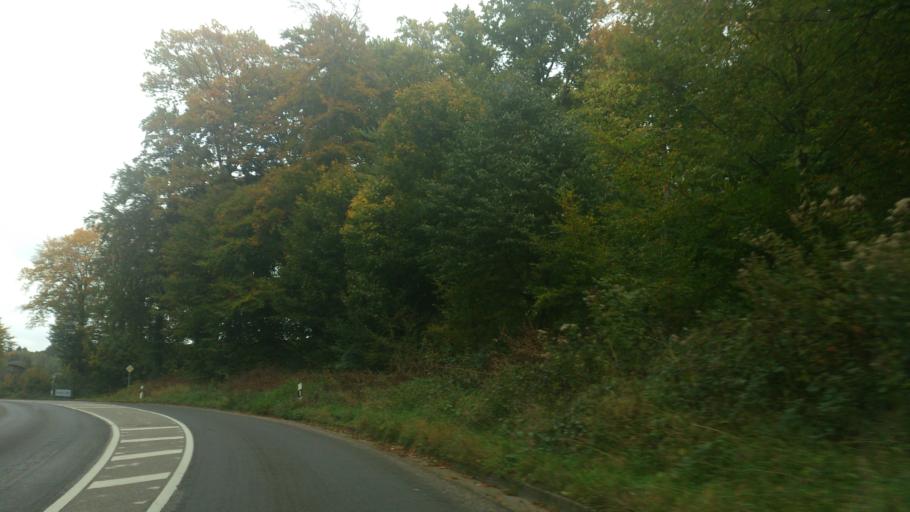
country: DE
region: Baden-Wuerttemberg
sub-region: Karlsruhe Region
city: Heidelberg
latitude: 49.3833
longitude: 8.7046
